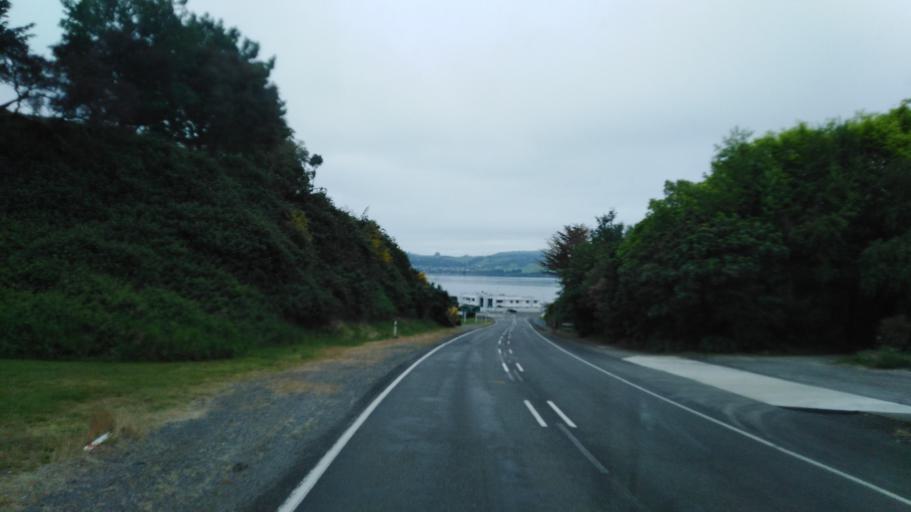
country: NZ
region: Waikato
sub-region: Taupo District
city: Taupo
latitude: -38.7057
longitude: 176.0908
